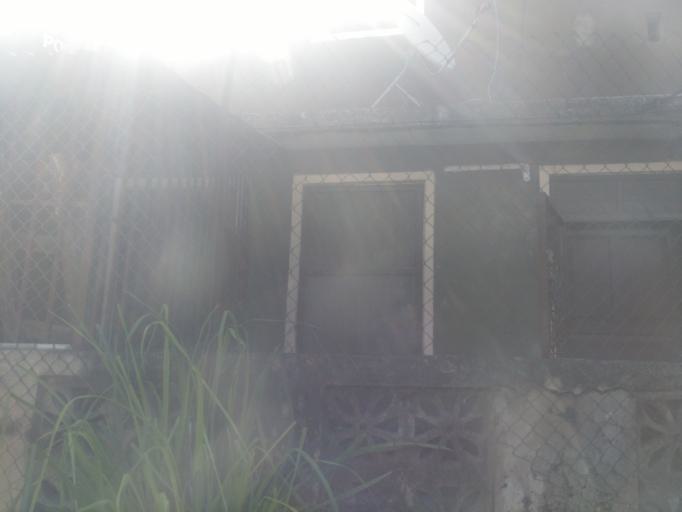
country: TZ
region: Zanzibar Urban/West
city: Zanzibar
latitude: -6.1574
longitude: 39.1936
